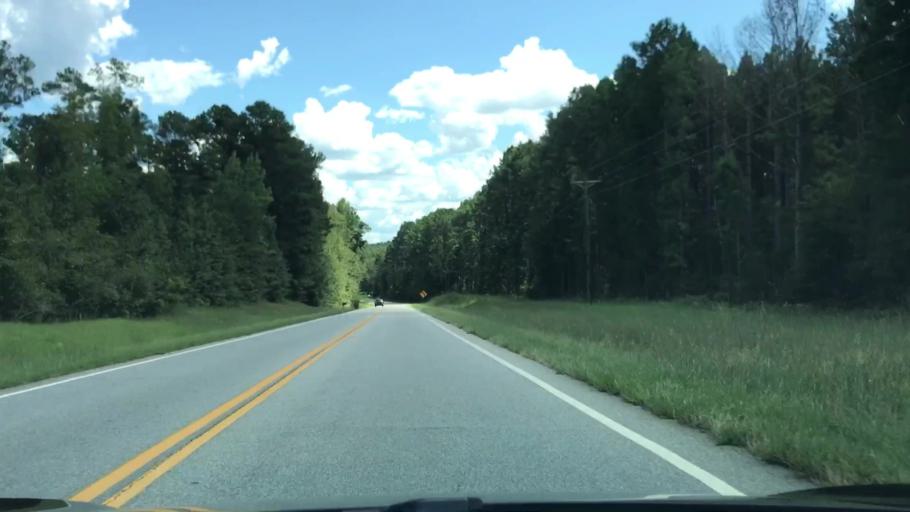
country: US
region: Georgia
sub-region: Greene County
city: Greensboro
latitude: 33.6753
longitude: -83.2671
